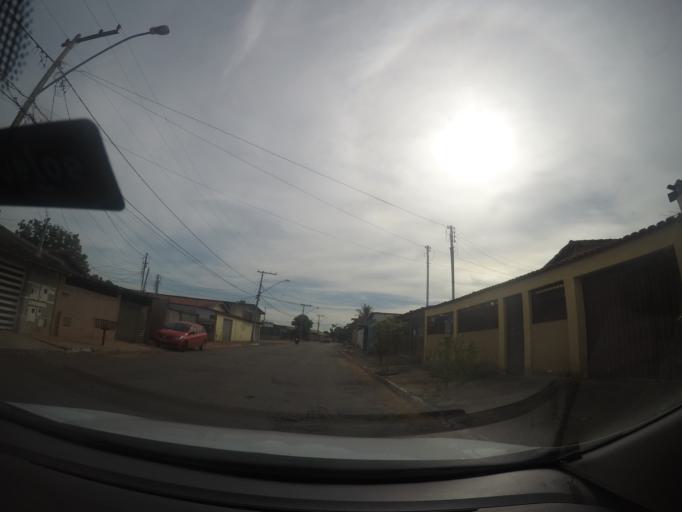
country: BR
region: Goias
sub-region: Goiania
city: Goiania
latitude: -16.6569
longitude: -49.3043
